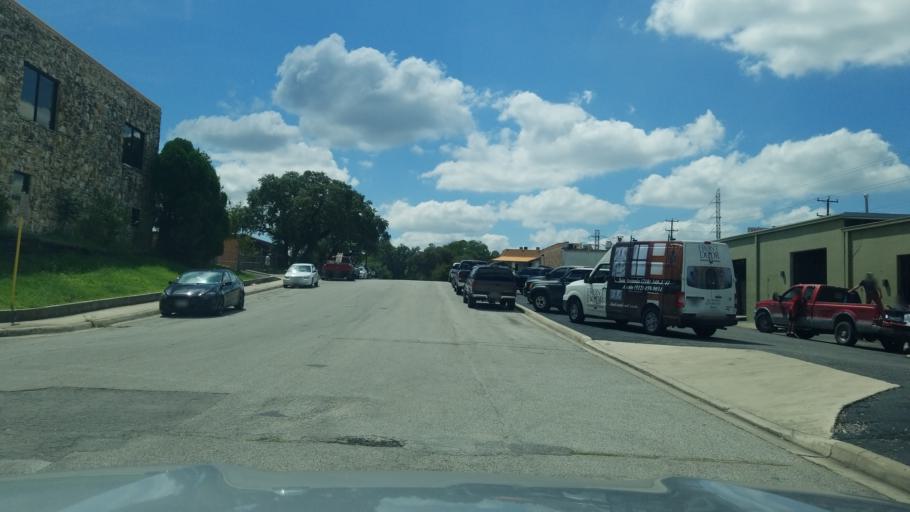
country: US
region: Texas
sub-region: Bexar County
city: Castle Hills
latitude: 29.5532
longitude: -98.5009
